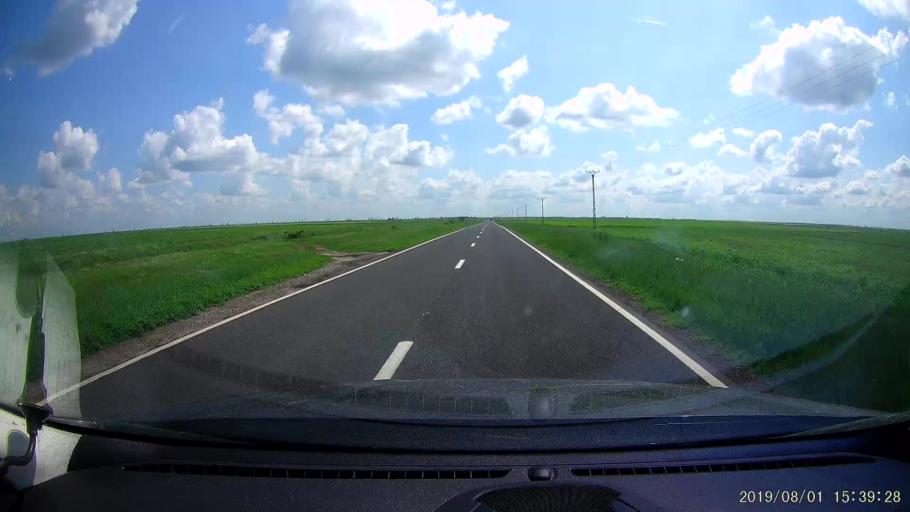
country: RO
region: Braila
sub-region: Comuna Victoria
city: Victoria
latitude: 44.8568
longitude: 27.5590
